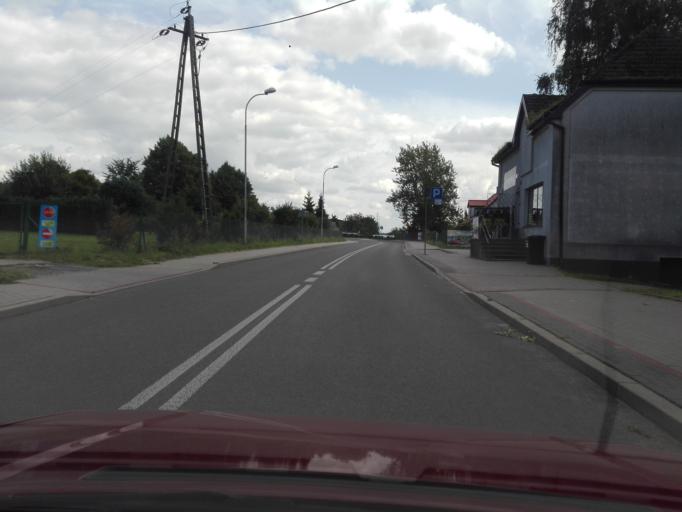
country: PL
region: West Pomeranian Voivodeship
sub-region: Powiat koszalinski
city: Sianow
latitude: 54.2957
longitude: 16.2770
